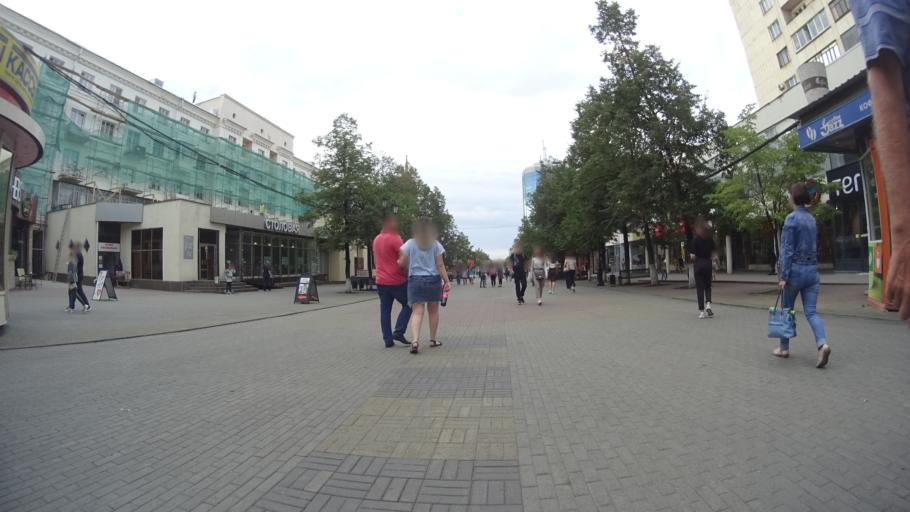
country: RU
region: Chelyabinsk
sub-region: Gorod Chelyabinsk
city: Chelyabinsk
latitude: 55.1616
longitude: 61.4008
